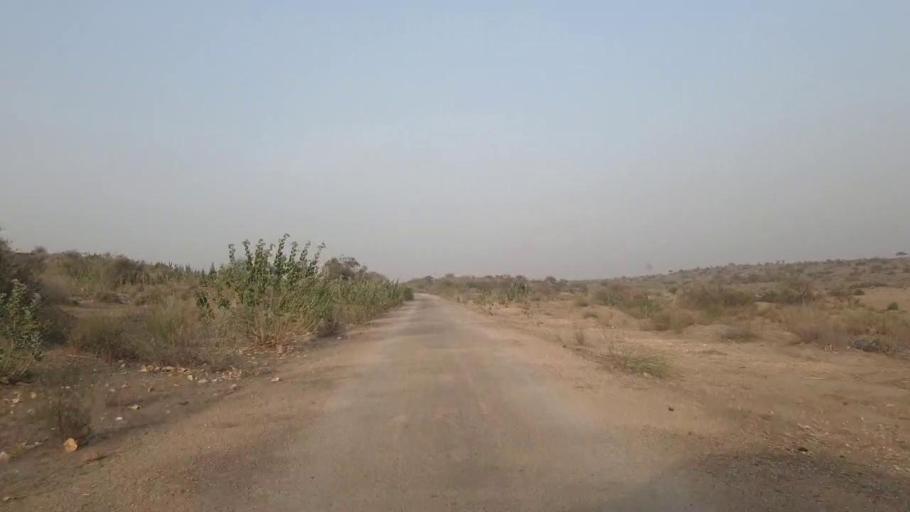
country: PK
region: Sindh
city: Chor
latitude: 25.5043
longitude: 69.9352
